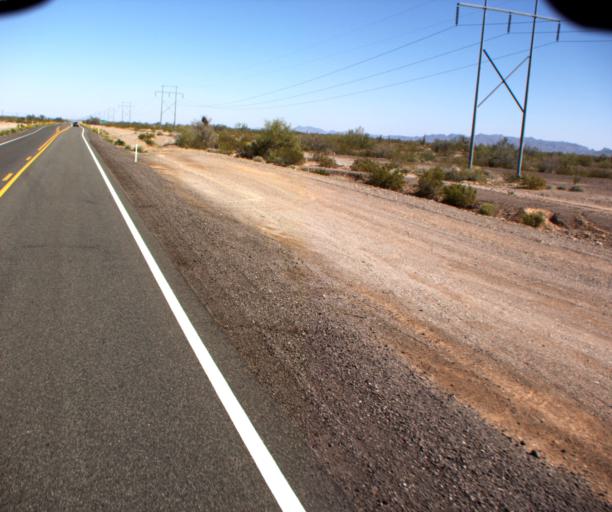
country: US
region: Arizona
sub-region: La Paz County
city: Quartzsite
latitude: 33.5773
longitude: -114.2170
